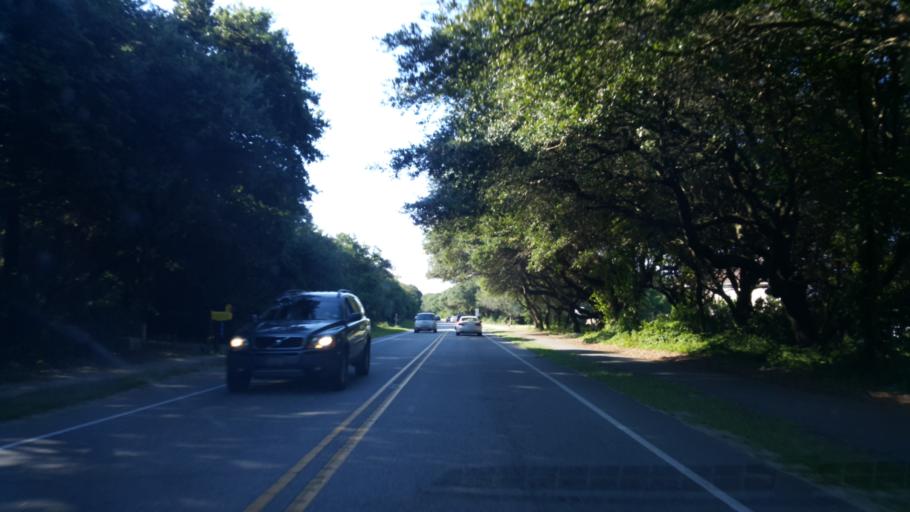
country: US
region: North Carolina
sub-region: Dare County
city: Southern Shores
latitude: 36.1385
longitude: -75.7364
